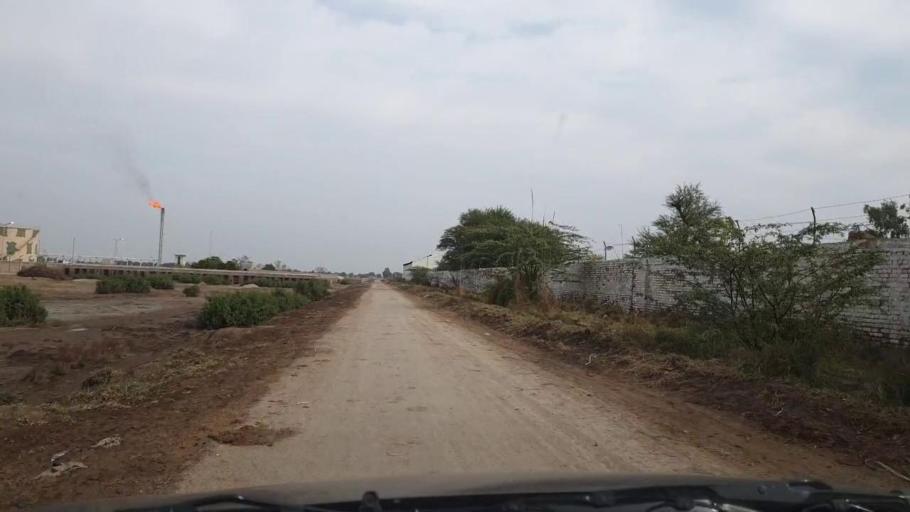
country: PK
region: Sindh
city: Sanghar
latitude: 26.0901
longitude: 68.8773
